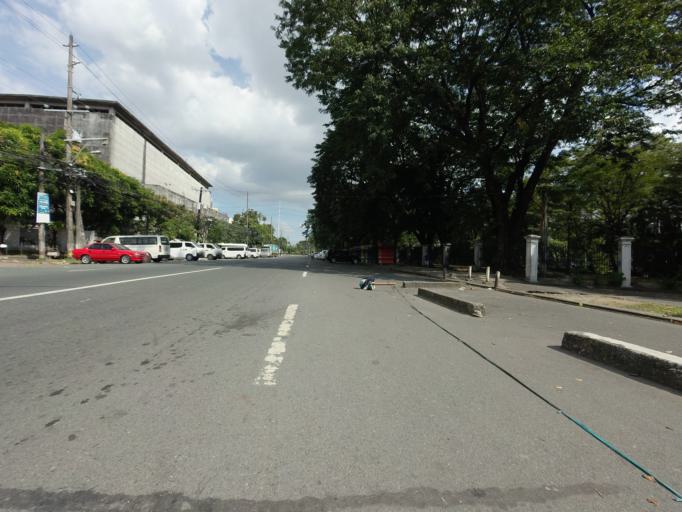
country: PH
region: Metro Manila
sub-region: City of Manila
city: Quiapo
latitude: 14.5944
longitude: 120.9763
